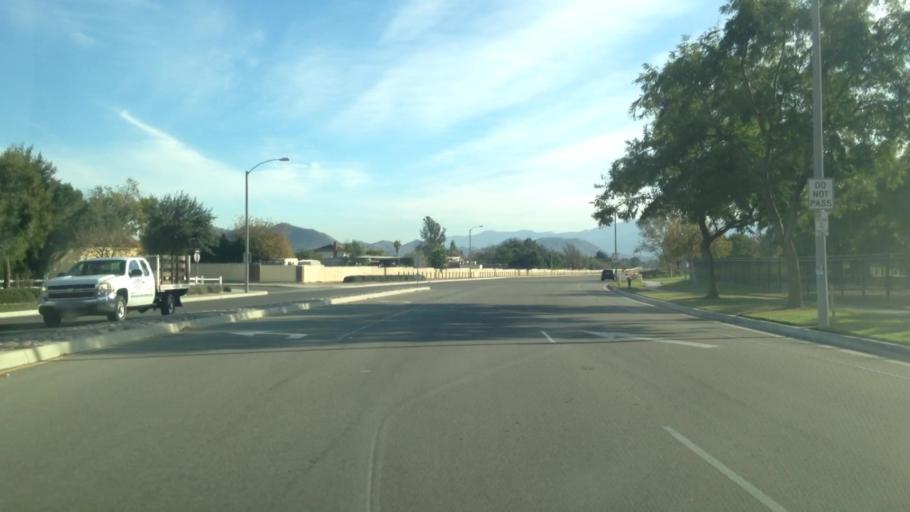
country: US
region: California
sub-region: Riverside County
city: Mira Loma
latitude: 33.9926
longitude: -117.5409
